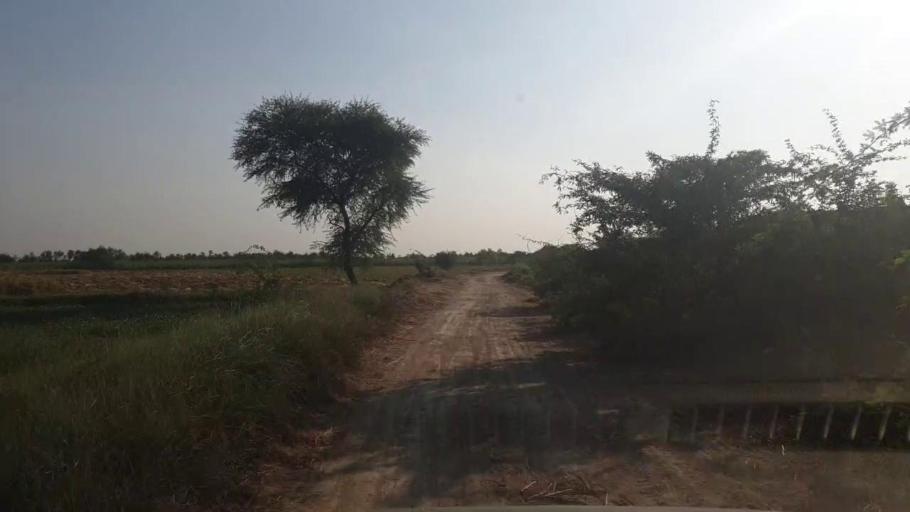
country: PK
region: Sindh
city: Badin
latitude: 24.6342
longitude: 68.7981
